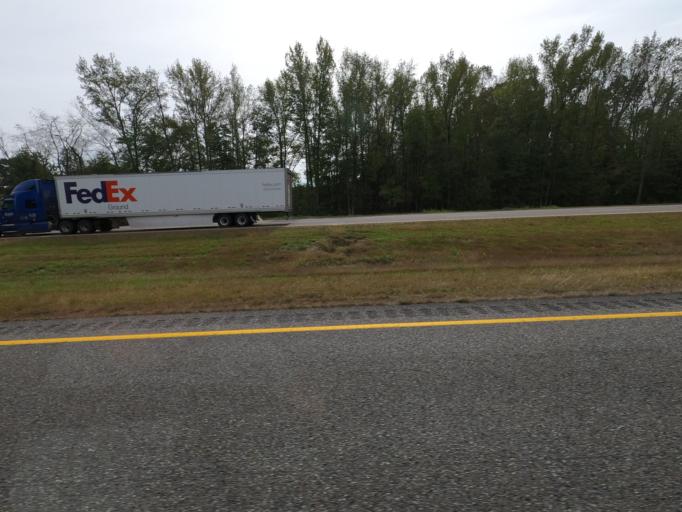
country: US
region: Tennessee
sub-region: Henderson County
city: Lexington
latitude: 35.7589
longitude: -88.4943
